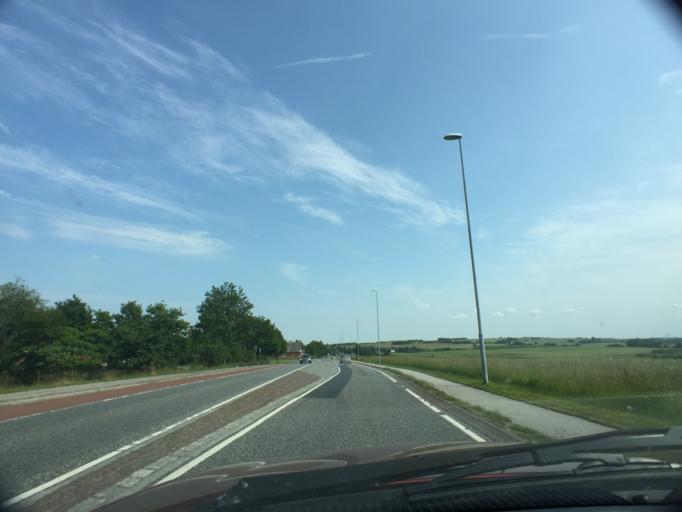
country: DK
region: Central Jutland
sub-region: Arhus Kommune
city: Sabro
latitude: 56.2236
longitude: 9.9680
